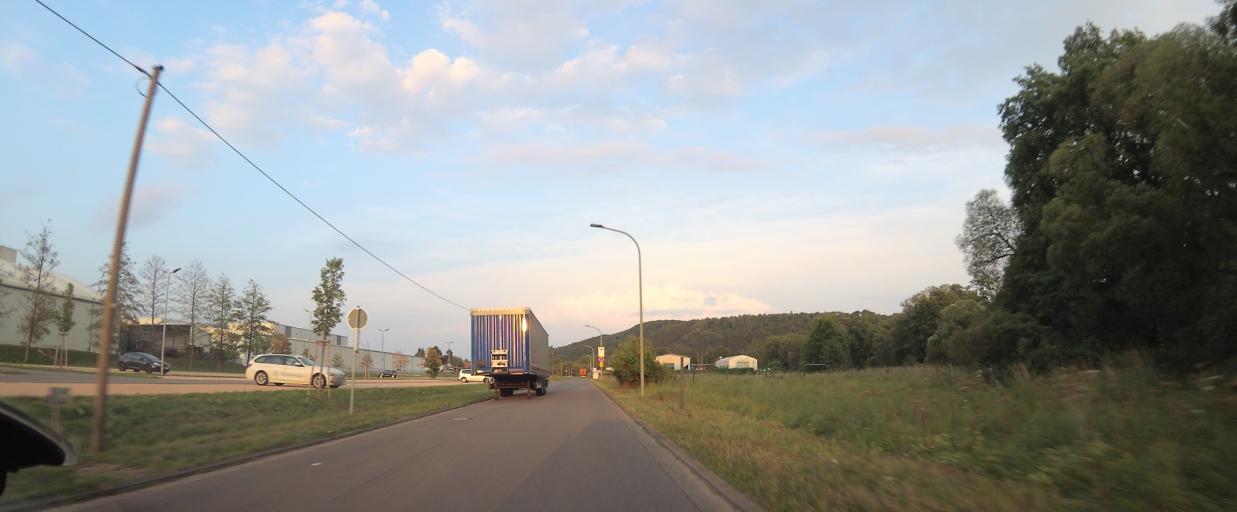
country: DE
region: Saarland
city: Wadern
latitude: 49.5241
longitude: 6.9026
